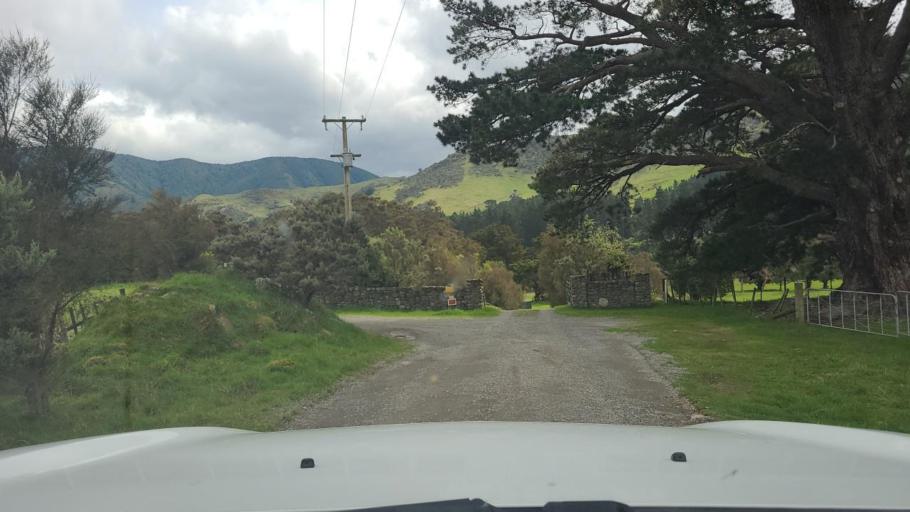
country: NZ
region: Wellington
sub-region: Masterton District
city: Masterton
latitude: -40.8848
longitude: 175.5129
